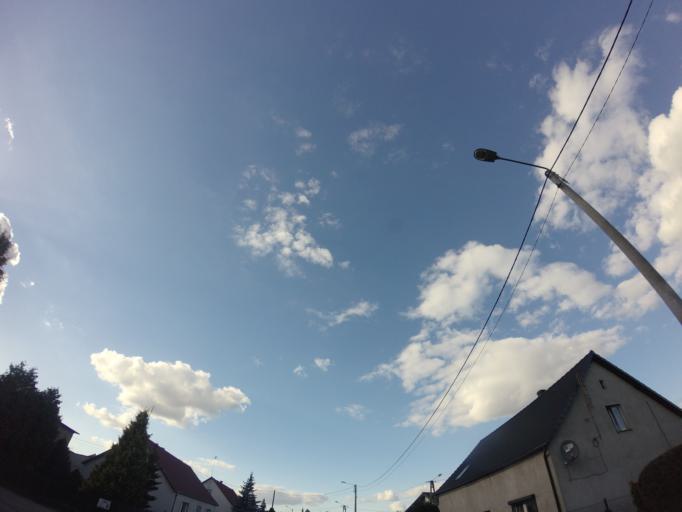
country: PL
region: Greater Poland Voivodeship
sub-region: Powiat nowotomyski
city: Nowy Tomysl
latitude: 52.2650
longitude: 16.1370
